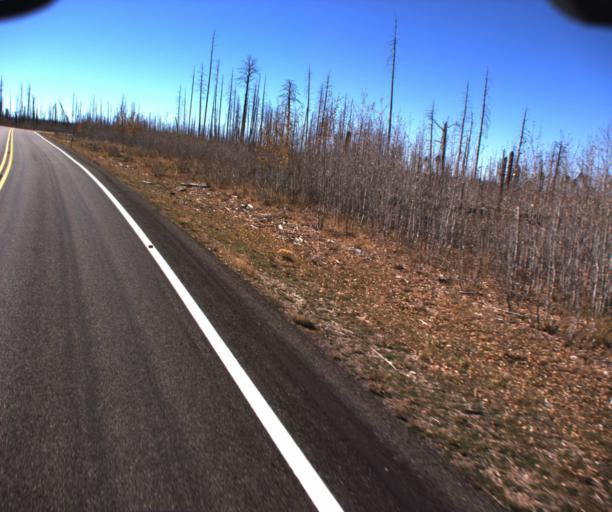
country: US
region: Arizona
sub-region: Coconino County
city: Grand Canyon
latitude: 36.5567
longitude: -112.1726
